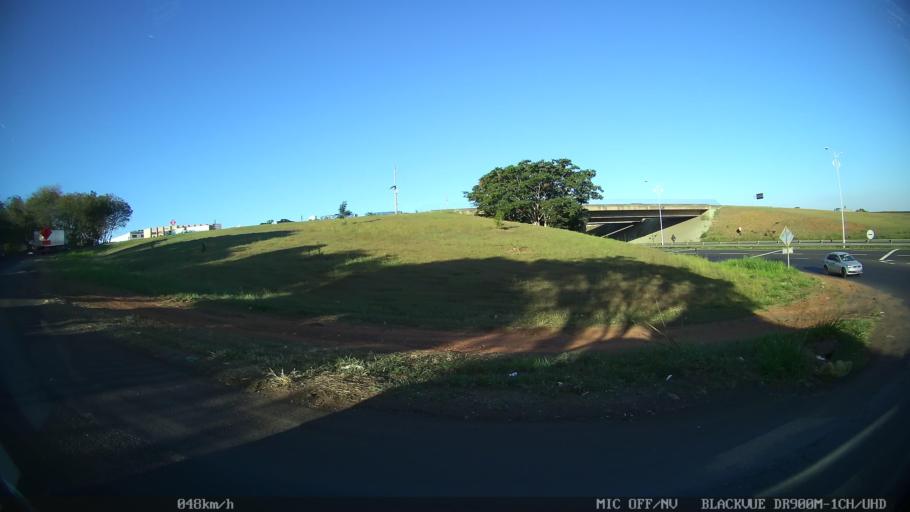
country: BR
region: Sao Paulo
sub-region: Sao Jose Do Rio Preto
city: Sao Jose do Rio Preto
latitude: -20.8023
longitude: -49.3565
